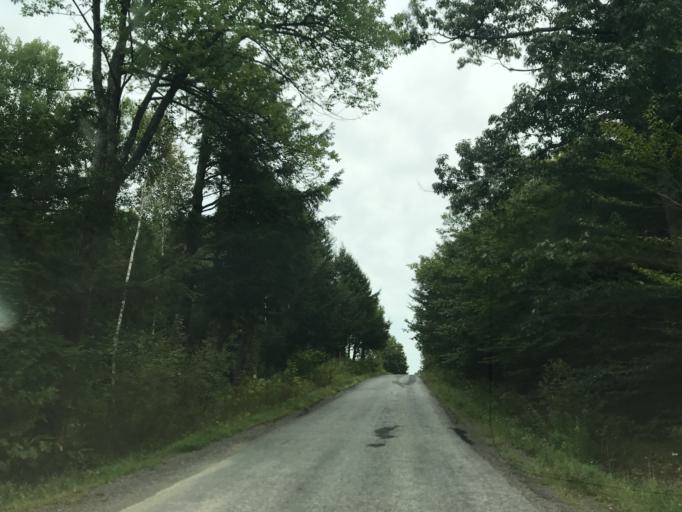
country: US
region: New York
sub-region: Otsego County
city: Worcester
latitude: 42.5948
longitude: -74.6884
